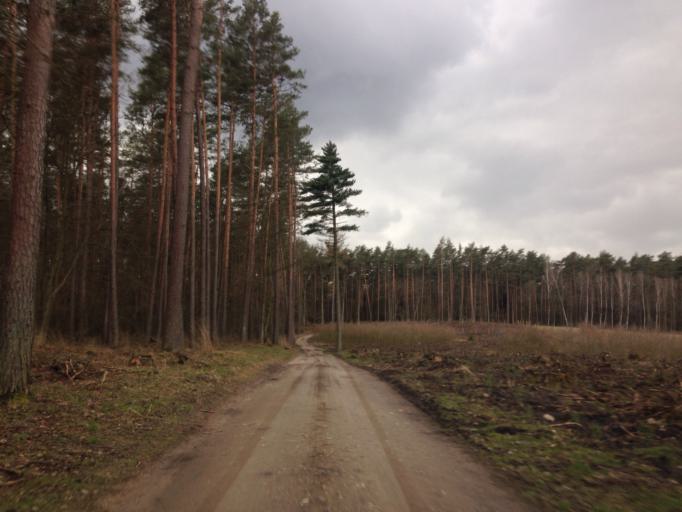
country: PL
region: Kujawsko-Pomorskie
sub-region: Powiat brodnicki
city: Gorzno
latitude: 53.1749
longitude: 19.6849
